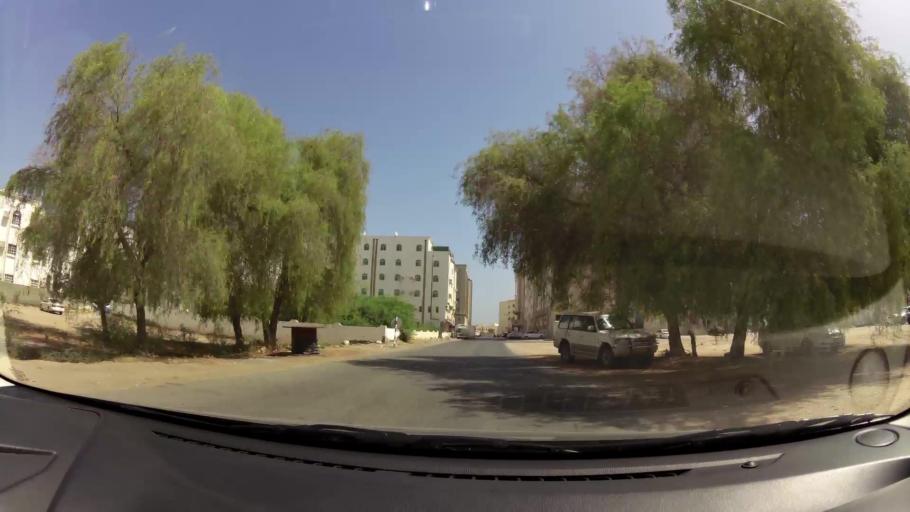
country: OM
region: Muhafazat Masqat
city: Bawshar
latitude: 23.5905
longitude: 58.4021
